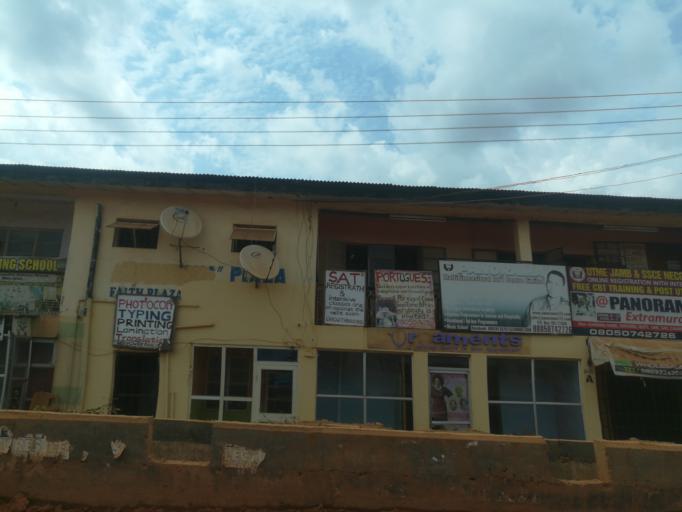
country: NG
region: Oyo
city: Ibadan
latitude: 7.4134
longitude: 3.9324
